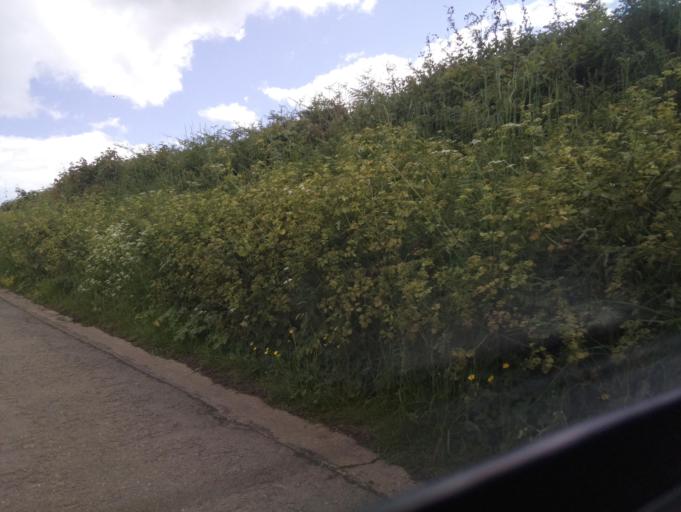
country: GB
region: England
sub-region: Devon
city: Dartmouth
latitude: 50.3631
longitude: -3.5500
